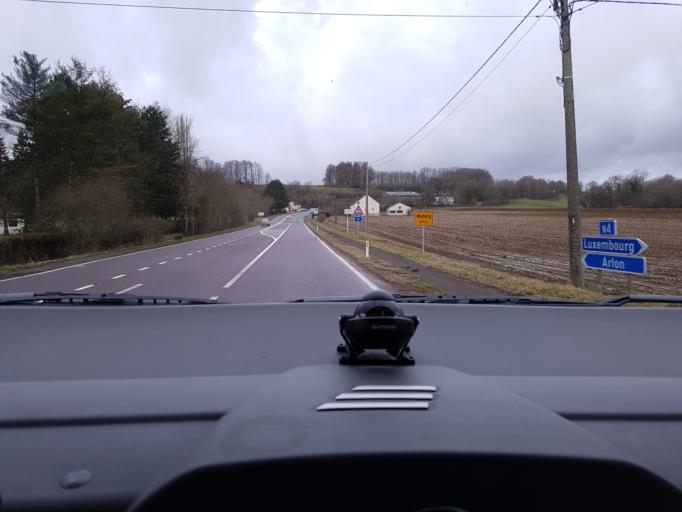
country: LU
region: Luxembourg
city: Eischen
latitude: 49.6578
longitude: 5.8607
